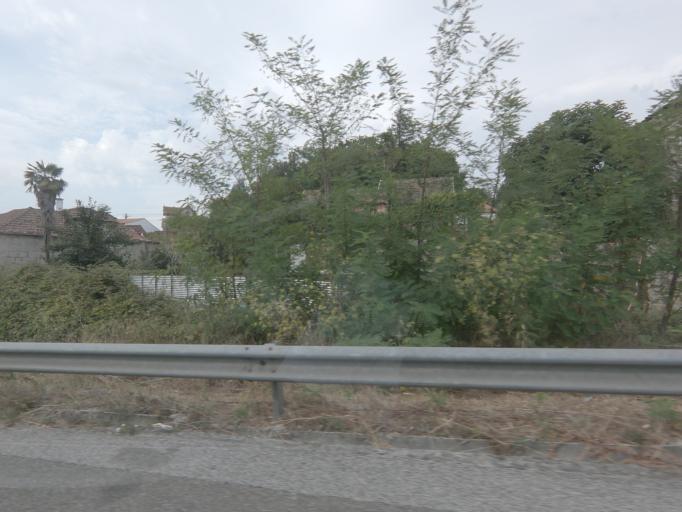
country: PT
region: Viseu
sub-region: Santa Comba Dao
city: Santa Comba Dao
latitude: 40.3873
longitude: -8.1243
